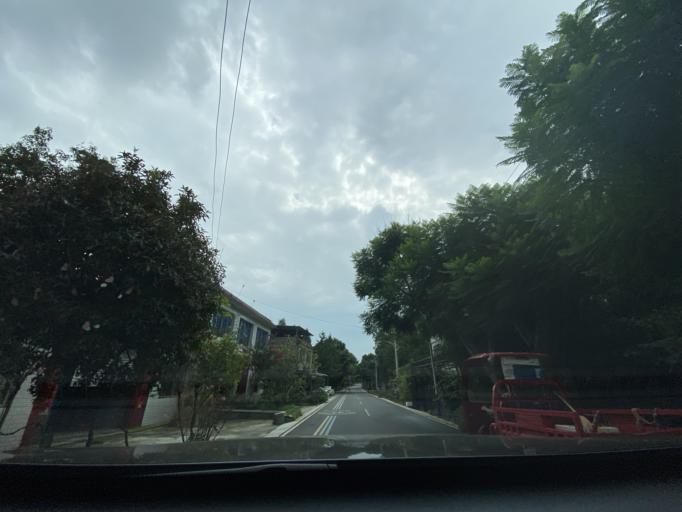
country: CN
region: Sichuan
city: Wujin
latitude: 30.4012
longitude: 103.9871
